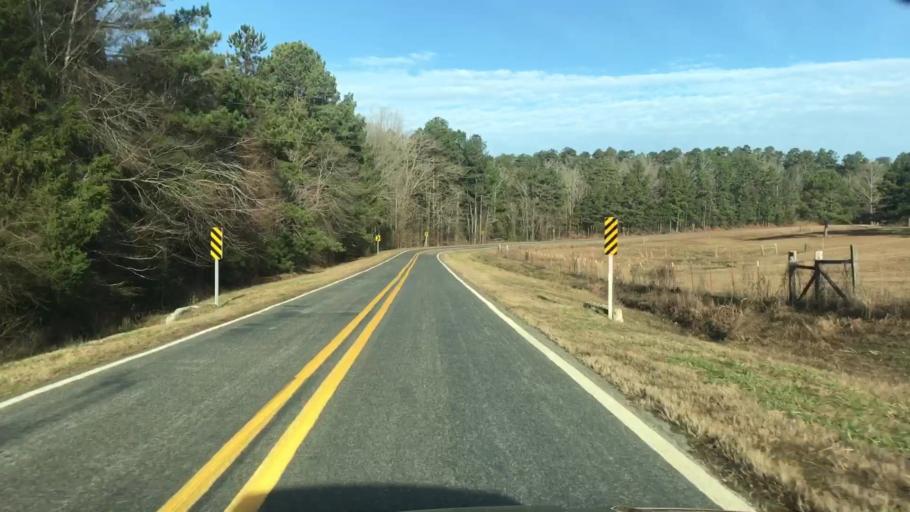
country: US
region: Arkansas
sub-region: Garland County
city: Rockwell
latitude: 34.4801
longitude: -93.2720
